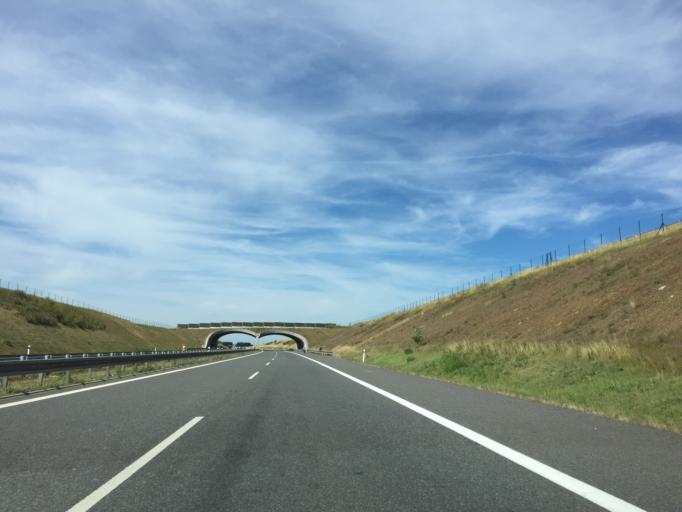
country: CZ
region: Jihocesky
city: Sobeslav
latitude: 49.3049
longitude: 14.7383
